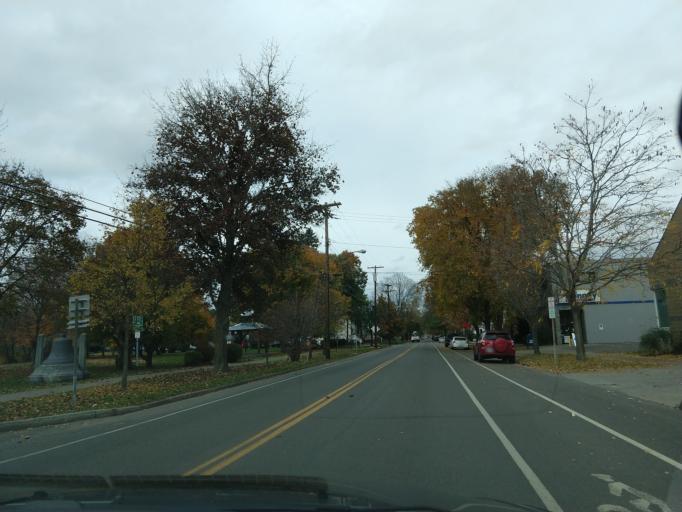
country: US
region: New York
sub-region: Tompkins County
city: Ithaca
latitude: 42.4451
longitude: -76.4993
